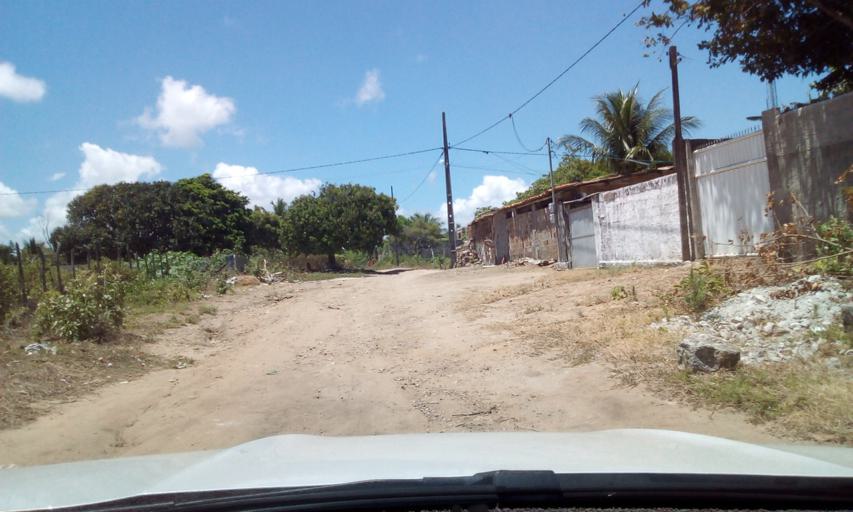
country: BR
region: Paraiba
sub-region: Joao Pessoa
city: Joao Pessoa
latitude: -7.1508
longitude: -34.8029
